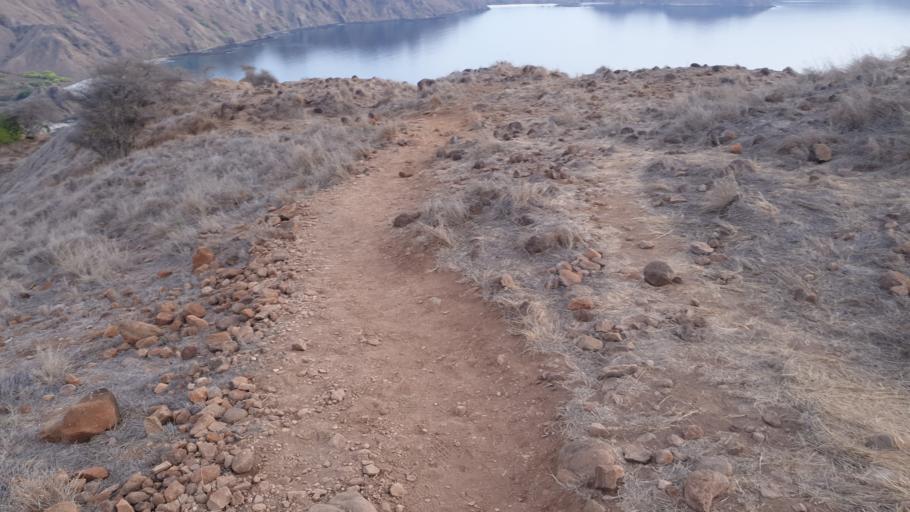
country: ID
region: East Nusa Tenggara
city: Komodo
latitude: -8.6821
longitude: 119.5573
